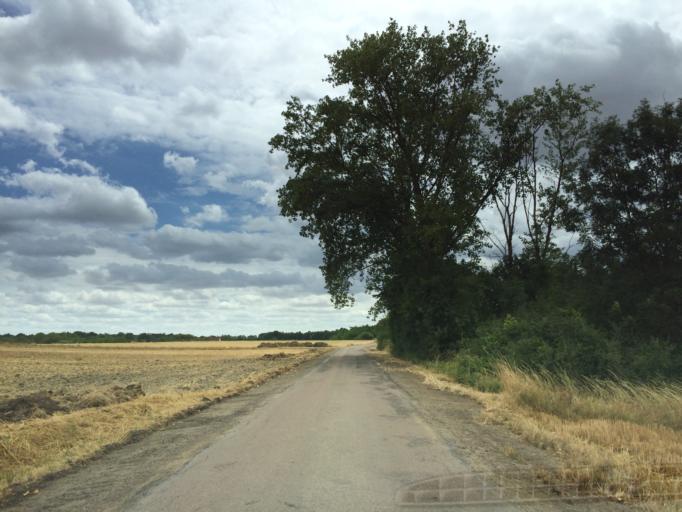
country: FR
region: Bourgogne
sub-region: Departement de l'Yonne
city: Fleury-la-Vallee
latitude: 47.8520
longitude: 3.4054
